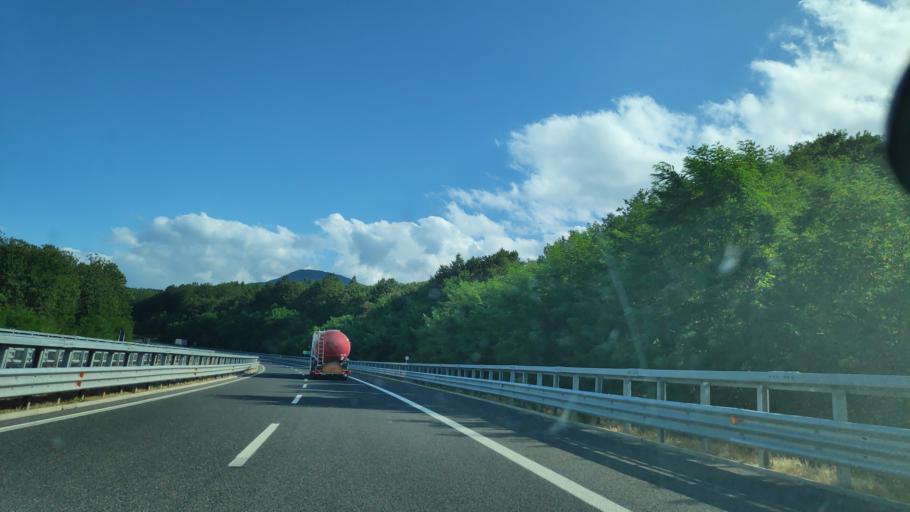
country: IT
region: Campania
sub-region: Provincia di Salerno
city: Casalbuono
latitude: 40.2400
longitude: 15.6597
